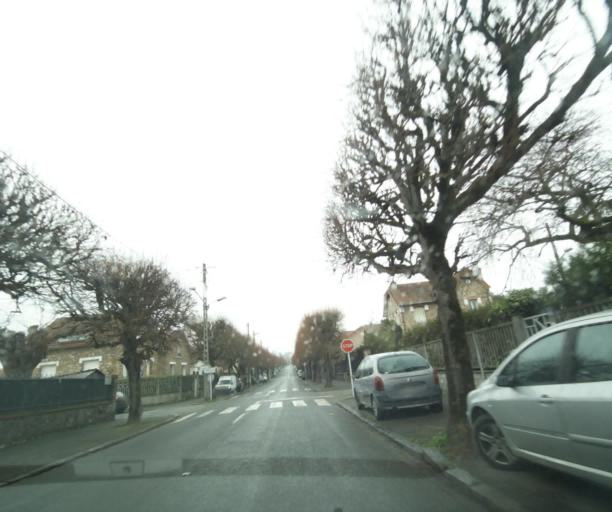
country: FR
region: Ile-de-France
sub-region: Departement du Val-de-Marne
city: Ablon-sur-Seine
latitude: 48.7376
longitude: 2.4207
